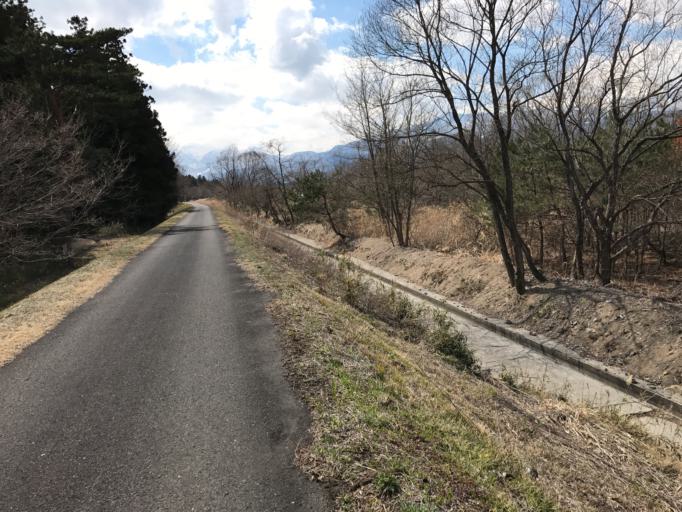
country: JP
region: Fukushima
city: Fukushima-shi
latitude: 37.7412
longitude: 140.3978
